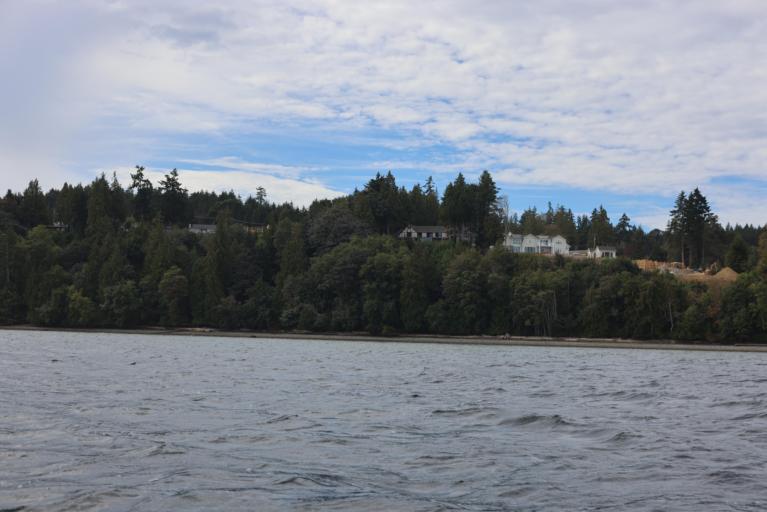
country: CA
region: British Columbia
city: Nanaimo
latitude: 49.2525
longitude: -124.0565
